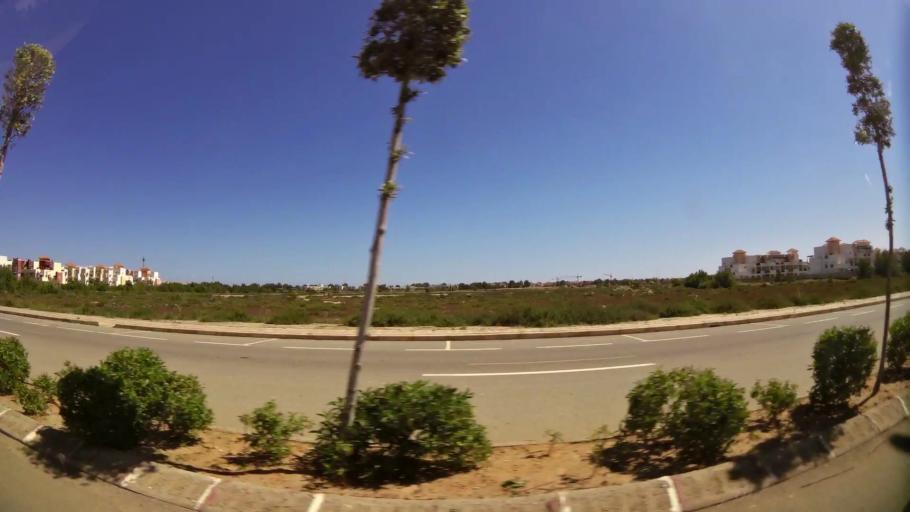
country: MA
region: Oriental
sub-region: Berkane-Taourirt
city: Madagh
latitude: 35.1018
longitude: -2.3112
